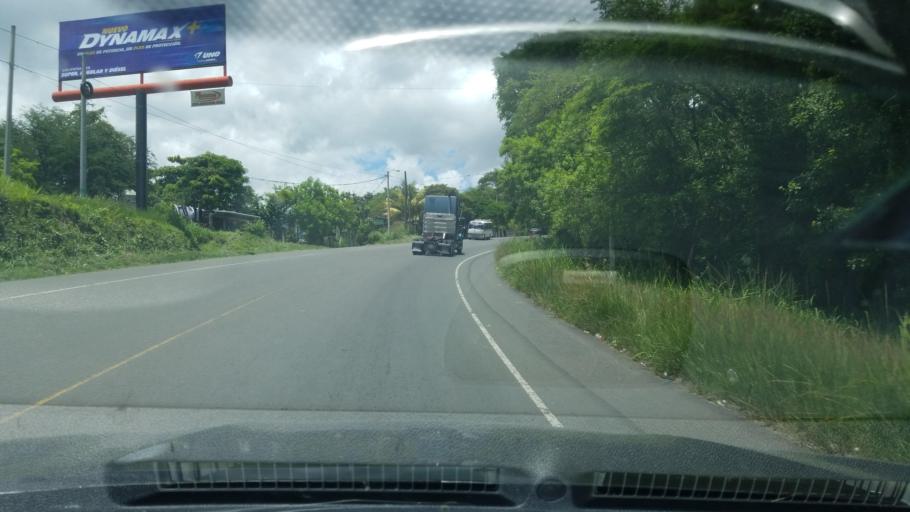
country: HN
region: Francisco Morazan
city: Rio Abajo
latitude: 14.1655
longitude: -87.2037
